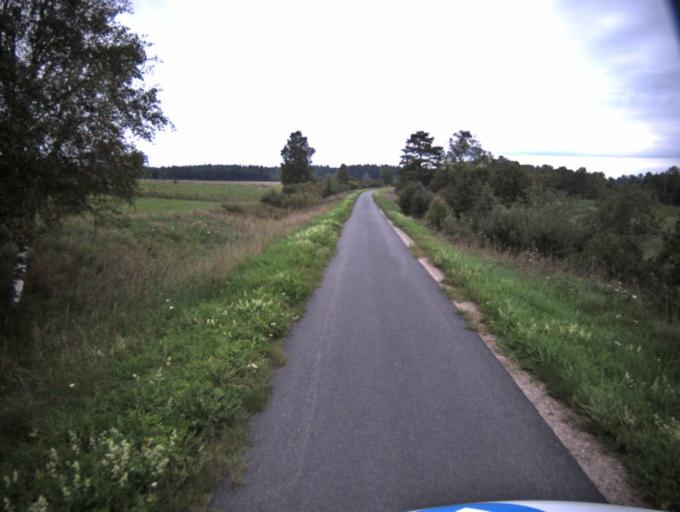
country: SE
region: Vaestra Goetaland
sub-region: Falkopings Kommun
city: Falkoeping
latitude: 57.9986
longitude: 13.5447
